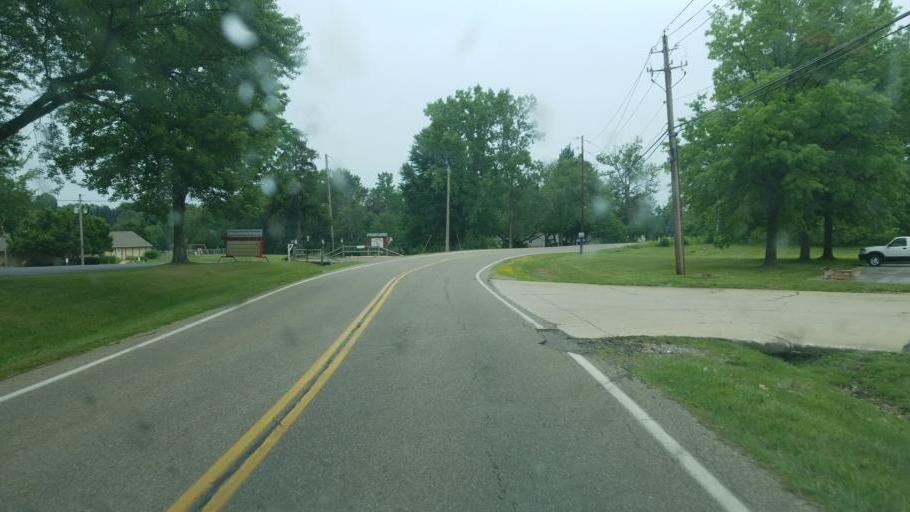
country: US
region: Ohio
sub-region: Summit County
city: Mogadore
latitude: 41.0661
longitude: -81.4171
